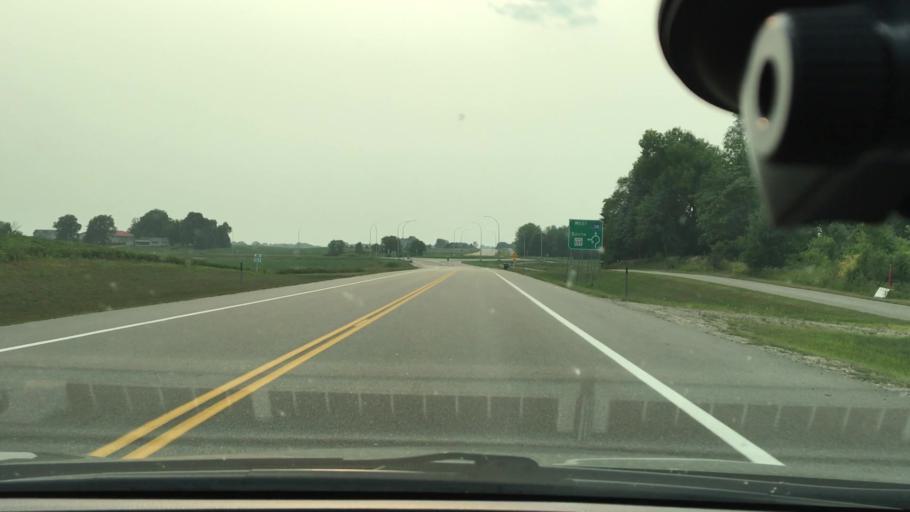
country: US
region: Minnesota
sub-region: Wright County
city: Otsego
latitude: 45.2524
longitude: -93.5966
